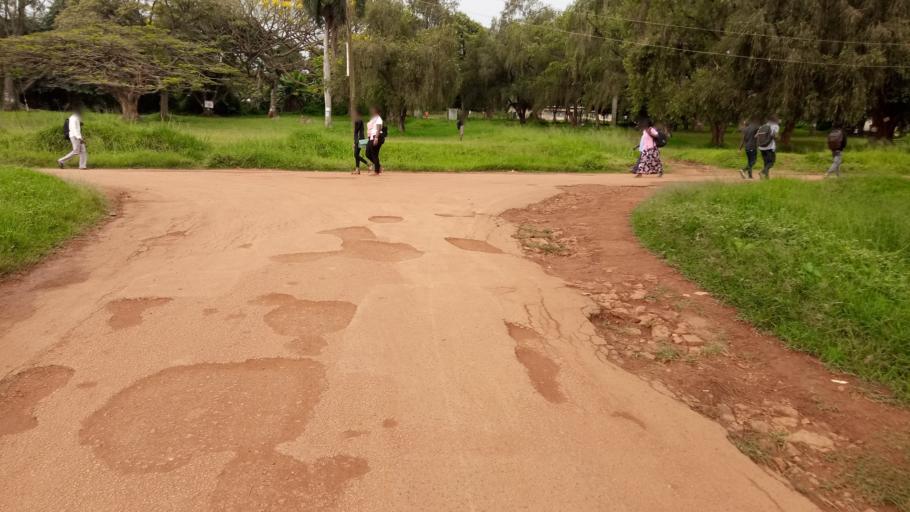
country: UG
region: Central Region
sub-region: Wakiso District
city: Kireka
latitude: 0.3498
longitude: 32.6283
